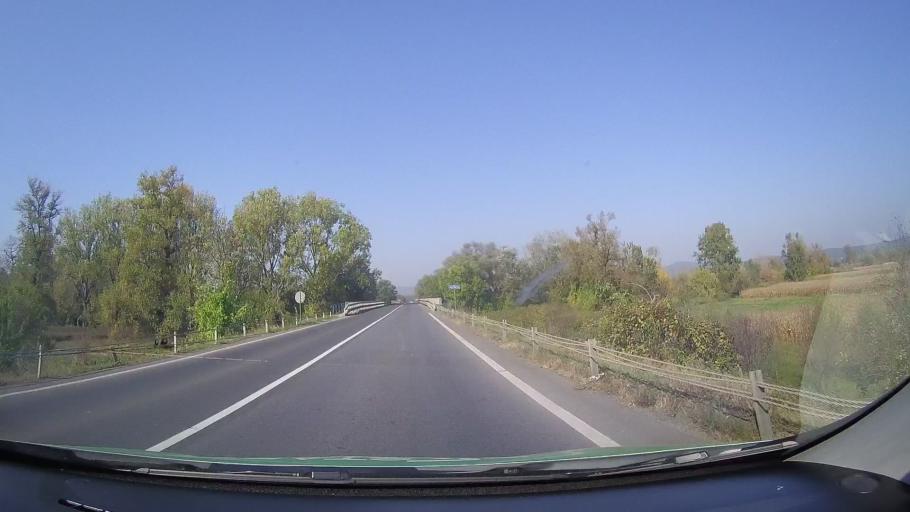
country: RO
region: Hunedoara
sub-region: Comuna Ilia
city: Ilia
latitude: 45.9236
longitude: 22.6702
